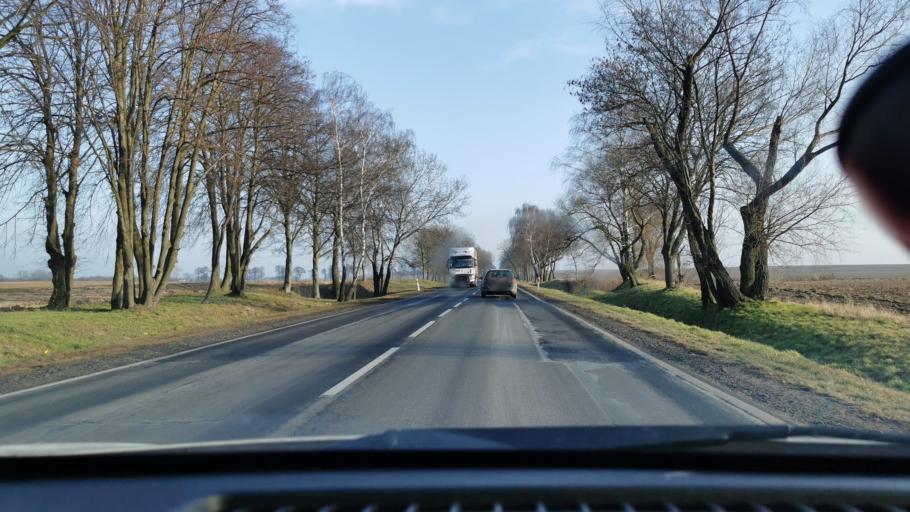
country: PL
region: Lodz Voivodeship
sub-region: Powiat sieradzki
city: Wroblew
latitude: 51.6228
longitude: 18.5775
